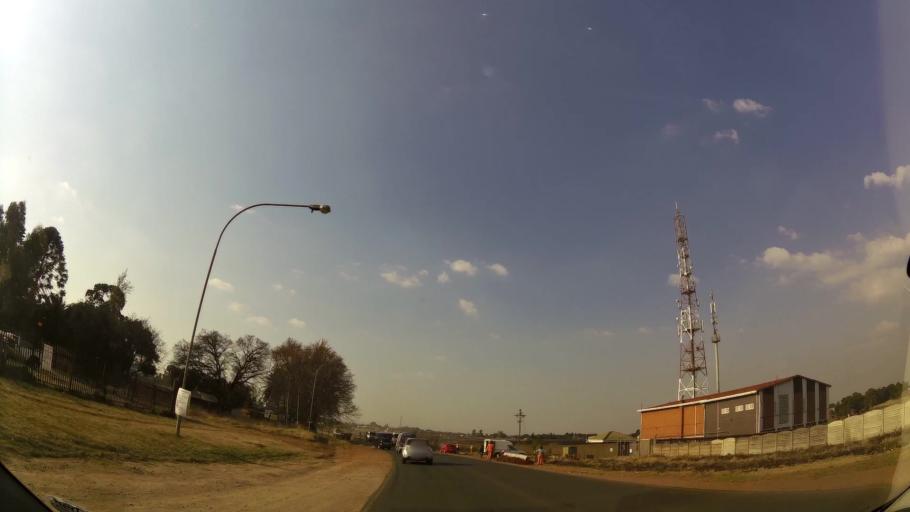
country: ZA
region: Gauteng
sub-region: Ekurhuleni Metropolitan Municipality
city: Tembisa
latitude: -26.0853
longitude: 28.2802
